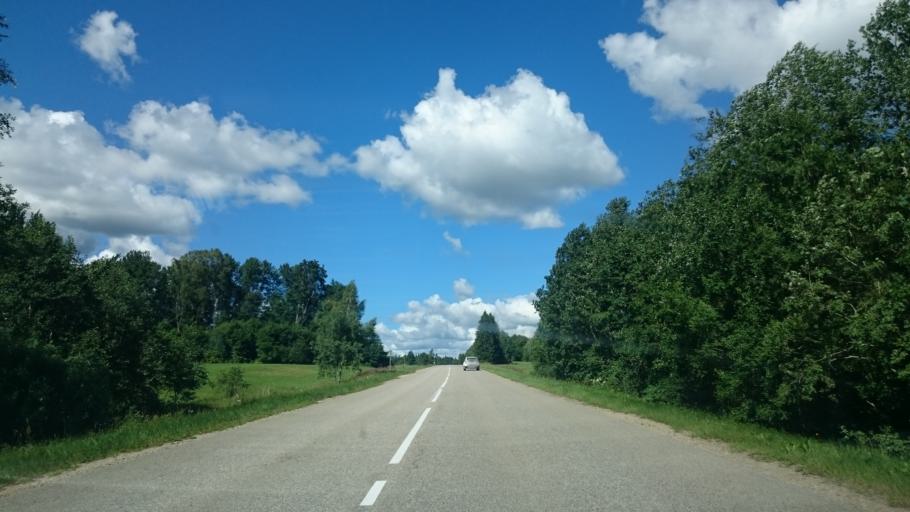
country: LV
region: Kuldigas Rajons
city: Kuldiga
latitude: 56.8657
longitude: 21.8535
